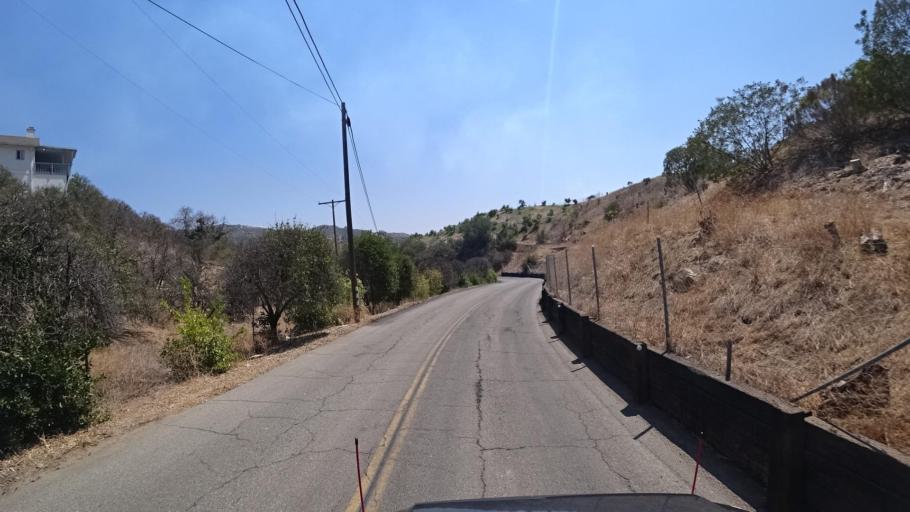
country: US
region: California
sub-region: San Diego County
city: Fallbrook
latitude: 33.4297
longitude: -117.3095
